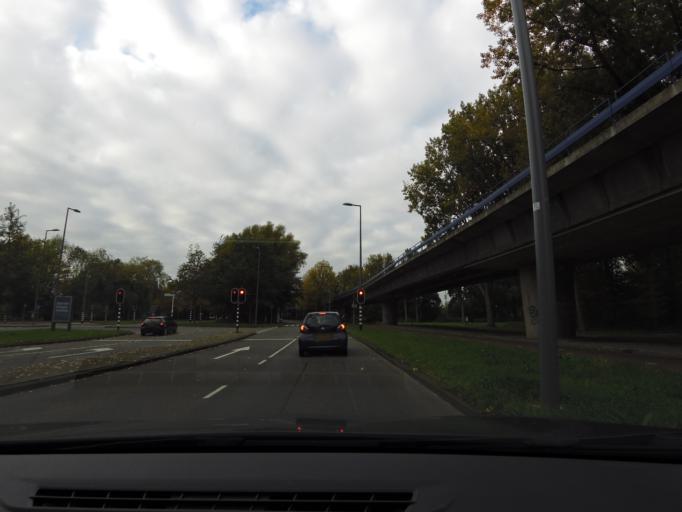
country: NL
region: South Holland
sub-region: Gemeente Rotterdam
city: Delfshaven
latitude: 51.8836
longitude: 4.4832
